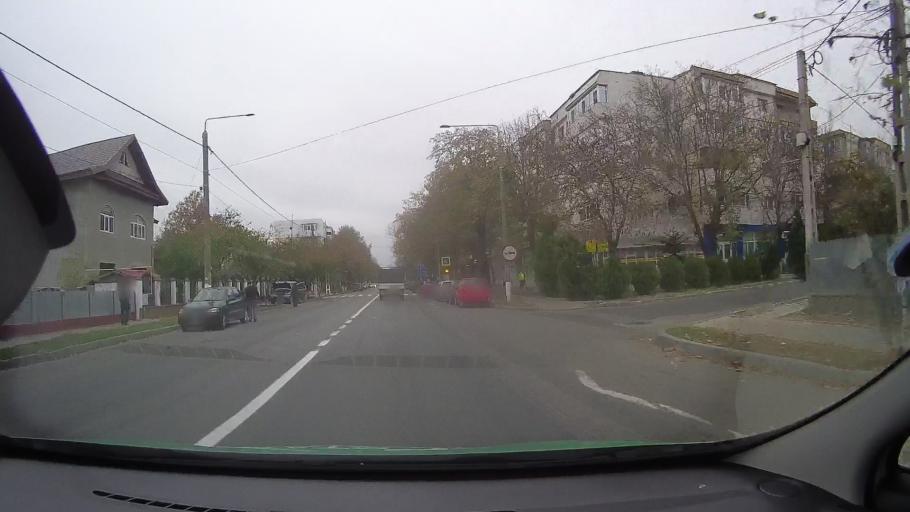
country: RO
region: Ialomita
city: Tandarei
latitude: 44.6399
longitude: 27.6651
